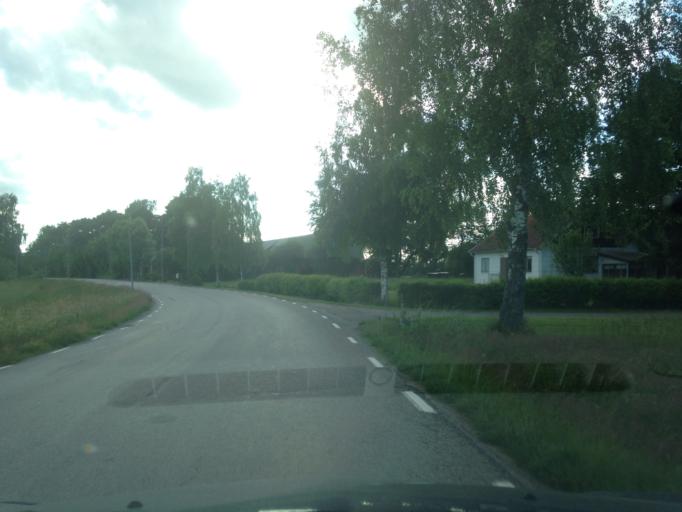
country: SE
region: Vaestra Goetaland
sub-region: Marks Kommun
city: Horred
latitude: 57.4769
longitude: 12.4069
